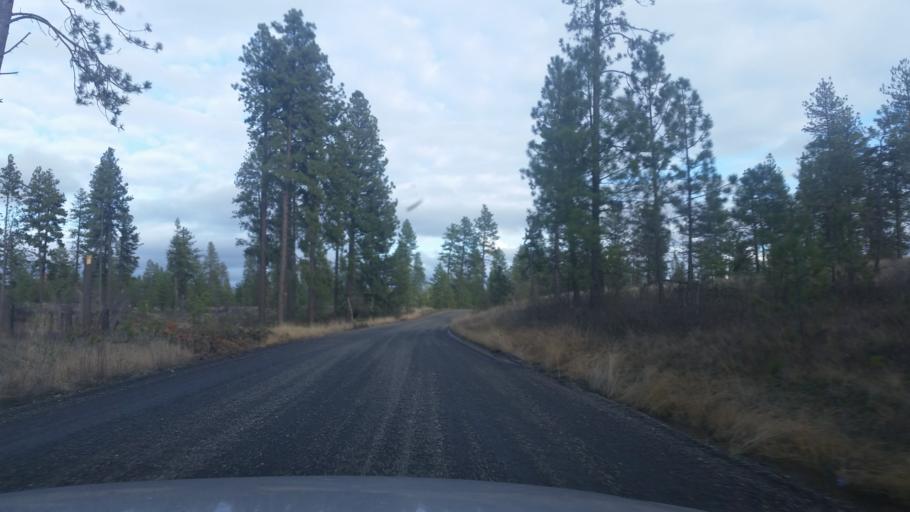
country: US
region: Washington
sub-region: Spokane County
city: Cheney
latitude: 47.4347
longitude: -117.4439
